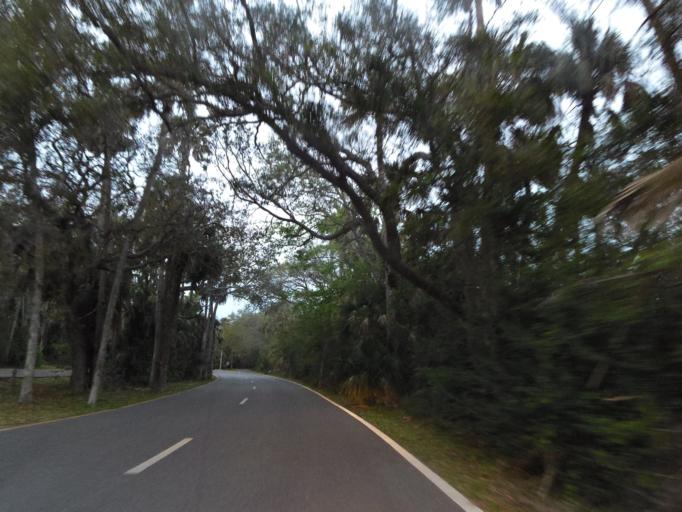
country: US
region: Florida
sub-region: Duval County
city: Atlantic Beach
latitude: 30.3700
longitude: -81.4001
